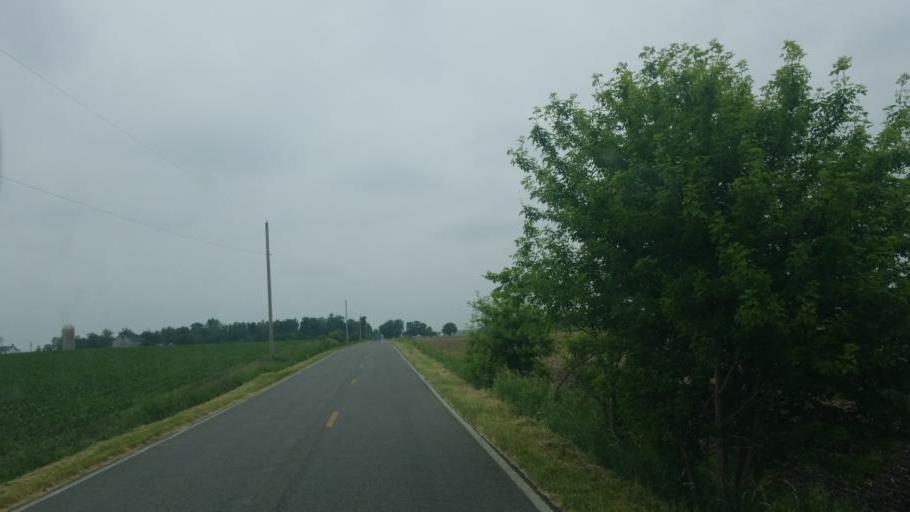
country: US
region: Indiana
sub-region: Marshall County
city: Bremen
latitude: 41.4864
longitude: -86.1178
